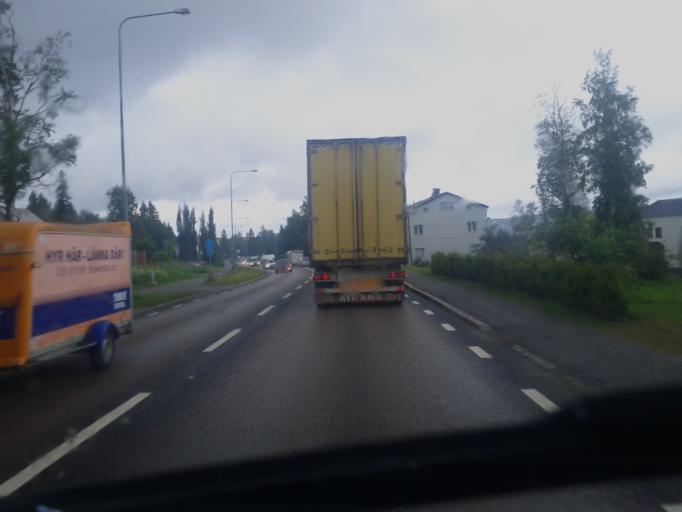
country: SE
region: Vaesternorrland
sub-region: Haernoesands Kommun
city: Haernoesand
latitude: 62.6201
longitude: 17.9129
